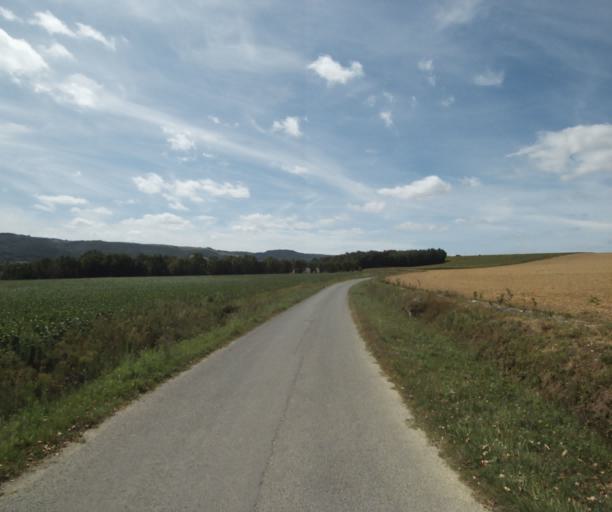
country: FR
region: Midi-Pyrenees
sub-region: Departement du Tarn
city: Soreze
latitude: 43.4792
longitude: 2.0767
